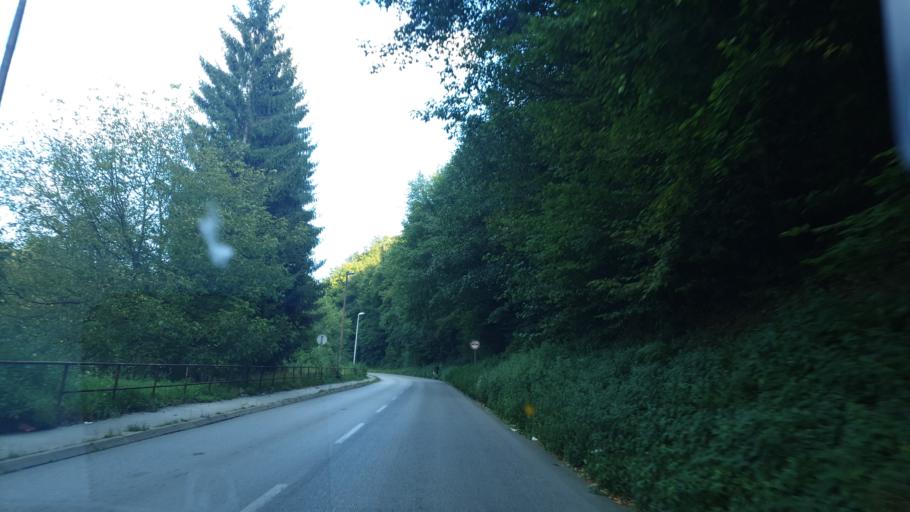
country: RS
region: Central Serbia
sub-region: Zlatiborski Okrug
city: Uzice
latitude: 43.8598
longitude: 19.8605
